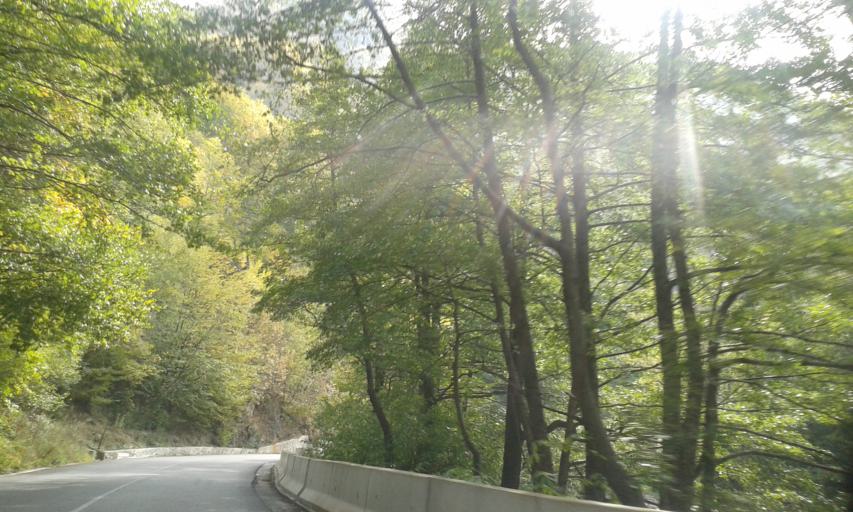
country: RO
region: Gorj
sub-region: Comuna Bumbesti-Jiu
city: Bumbesti-Jiu
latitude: 45.2396
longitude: 23.3940
